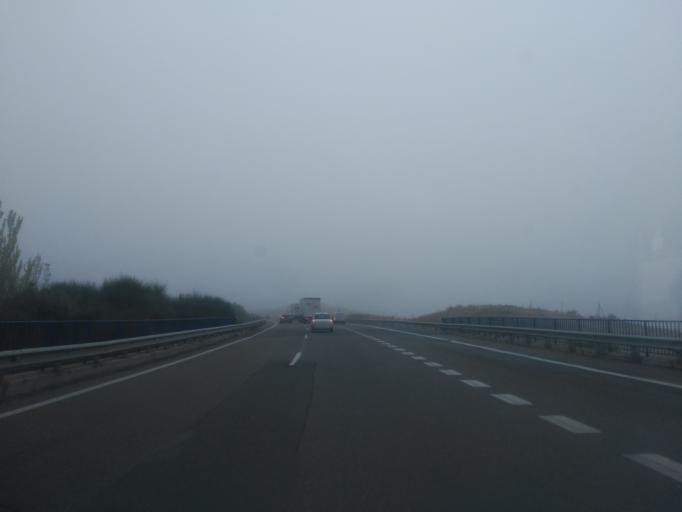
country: ES
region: Castille and Leon
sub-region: Provincia de Valladolid
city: Arroyo
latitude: 41.6165
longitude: -4.7907
